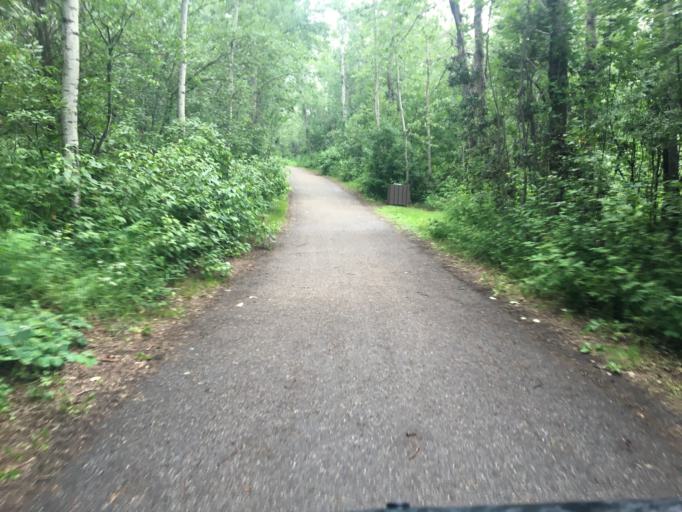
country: CA
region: Alberta
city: Grande Prairie
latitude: 55.1469
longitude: -118.7997
